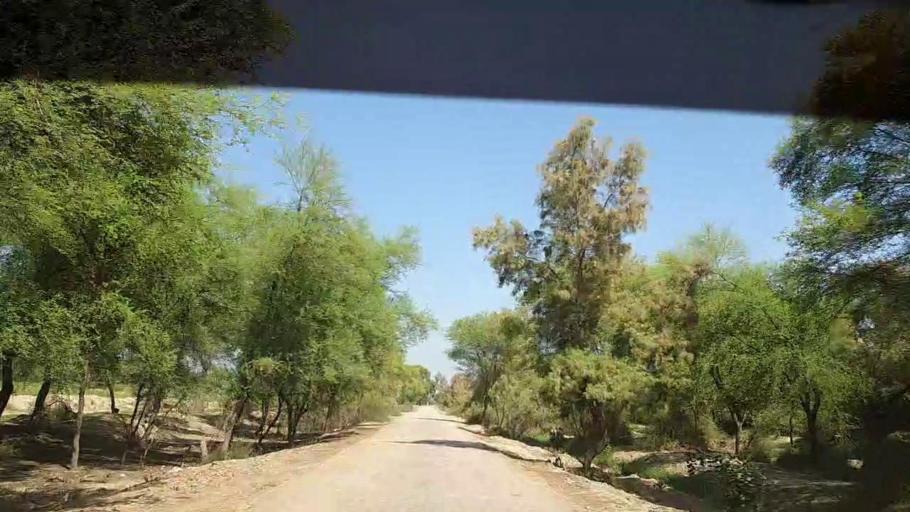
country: PK
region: Sindh
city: Tangwani
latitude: 28.2907
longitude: 69.0741
